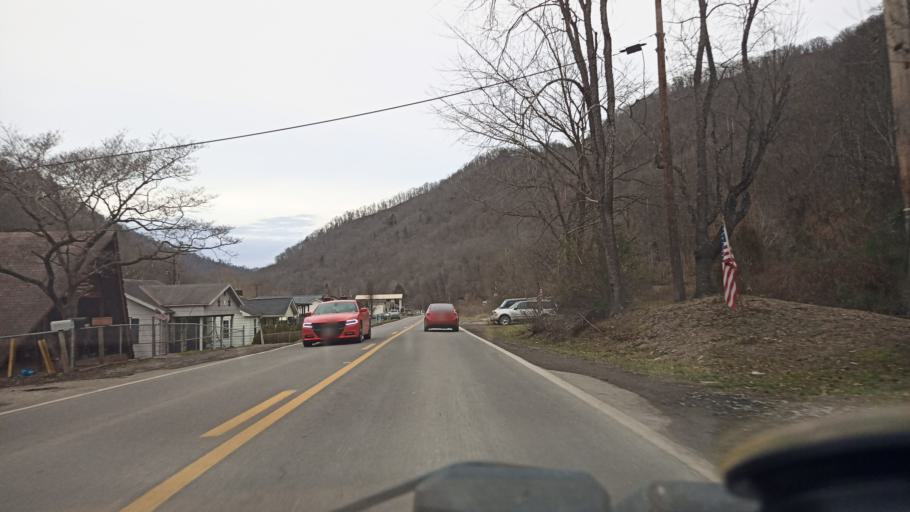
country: US
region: West Virginia
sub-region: Logan County
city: Mallory
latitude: 37.7129
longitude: -81.8676
